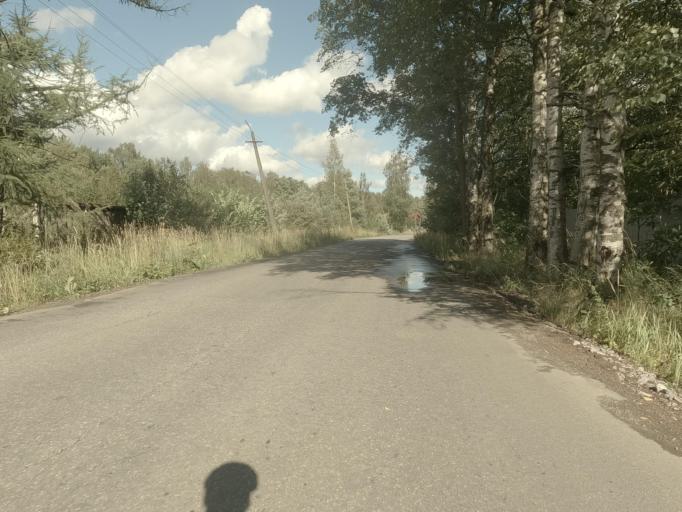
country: RU
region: Leningrad
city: Yanino Vtoroye
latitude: 59.9835
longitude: 30.5883
